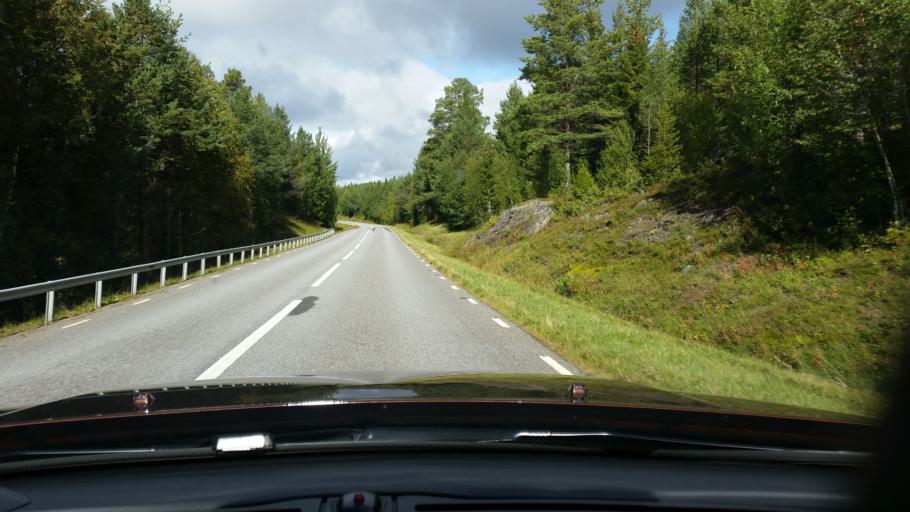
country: SE
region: Jaemtland
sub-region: Stroemsunds Kommun
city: Stroemsund
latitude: 64.3558
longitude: 14.6770
